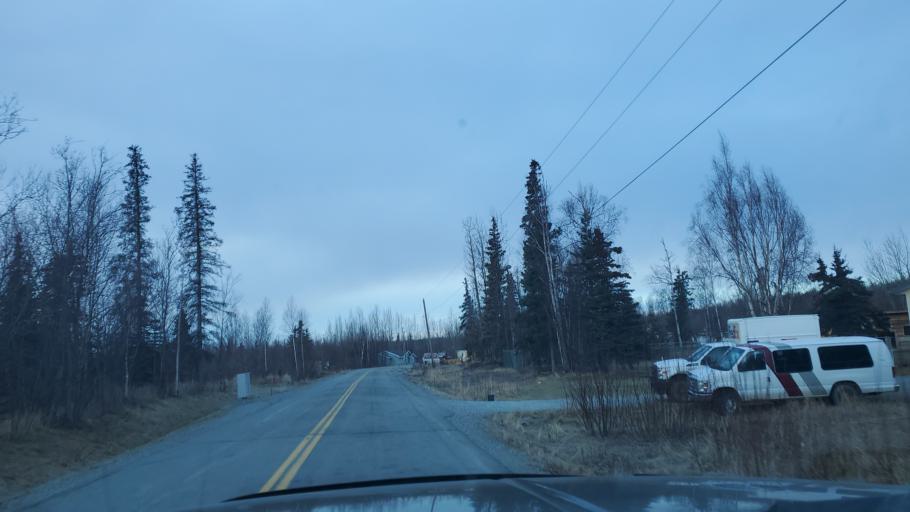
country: US
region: Alaska
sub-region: Matanuska-Susitna Borough
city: Lakes
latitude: 61.5724
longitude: -149.3317
